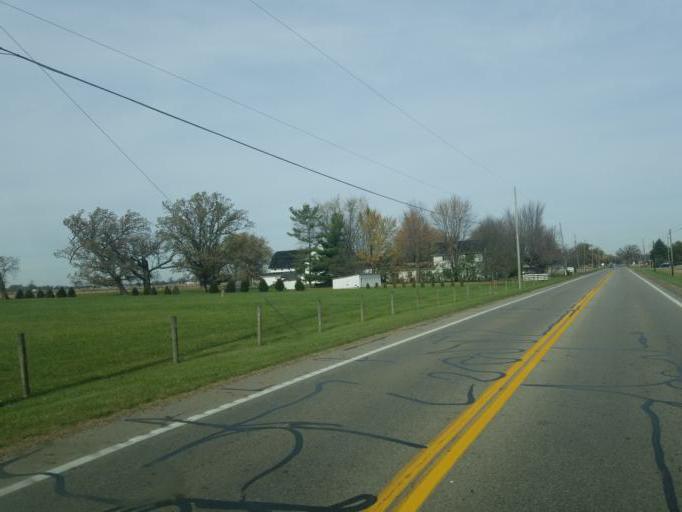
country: US
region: Ohio
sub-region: Madison County
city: Plain City
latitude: 40.0880
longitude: -83.2829
